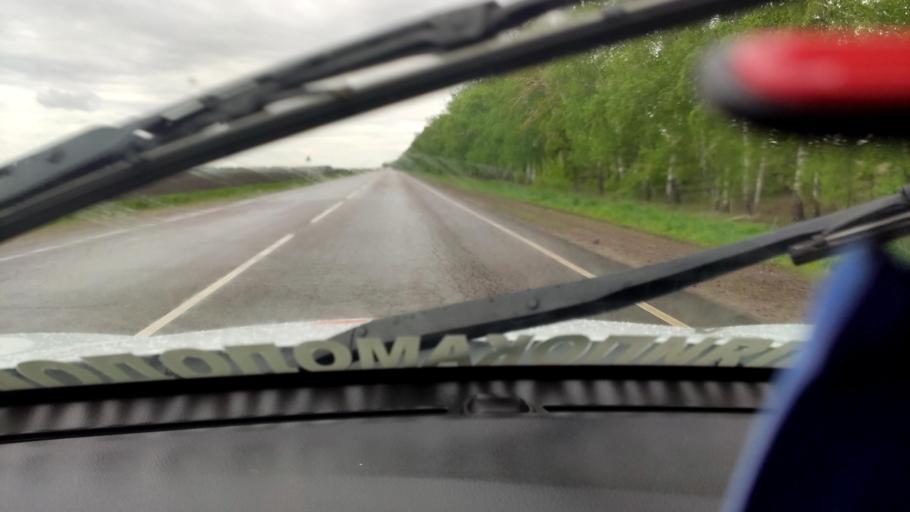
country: RU
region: Voronezj
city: Sredniy Ikorets
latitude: 51.0386
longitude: 39.6536
